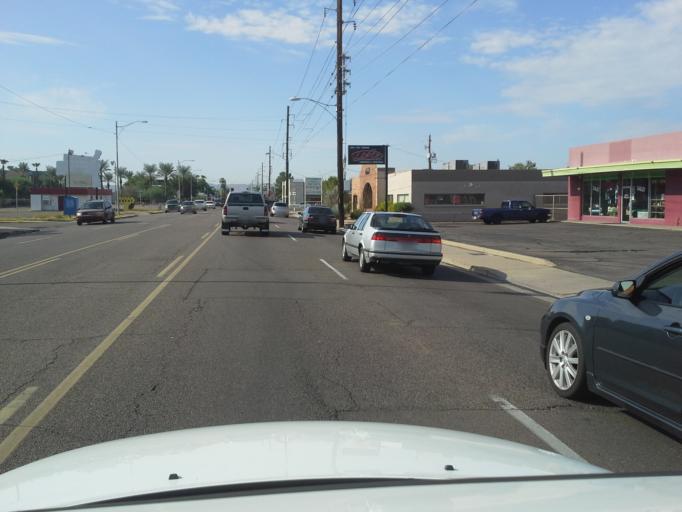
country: US
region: Arizona
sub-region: Maricopa County
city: Phoenix
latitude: 33.4900
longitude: -112.0477
